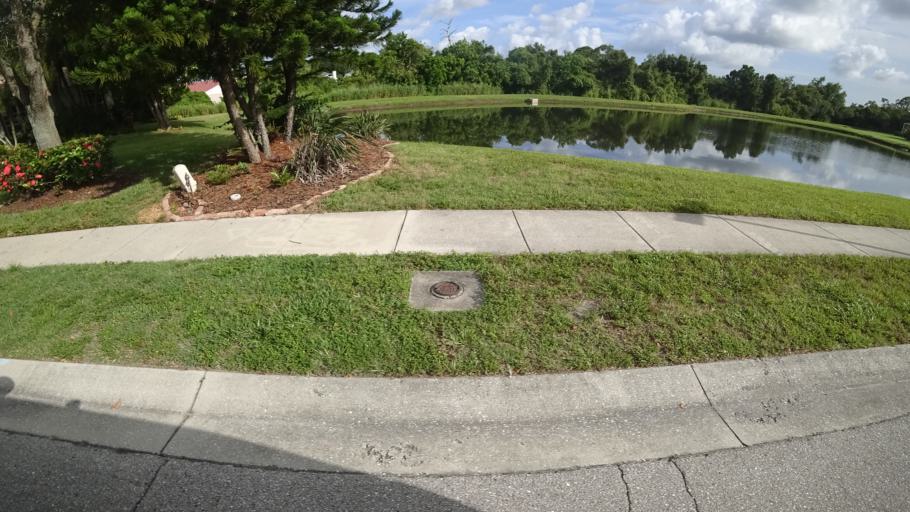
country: US
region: Florida
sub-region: Sarasota County
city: Desoto Lakes
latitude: 27.4149
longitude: -82.4806
